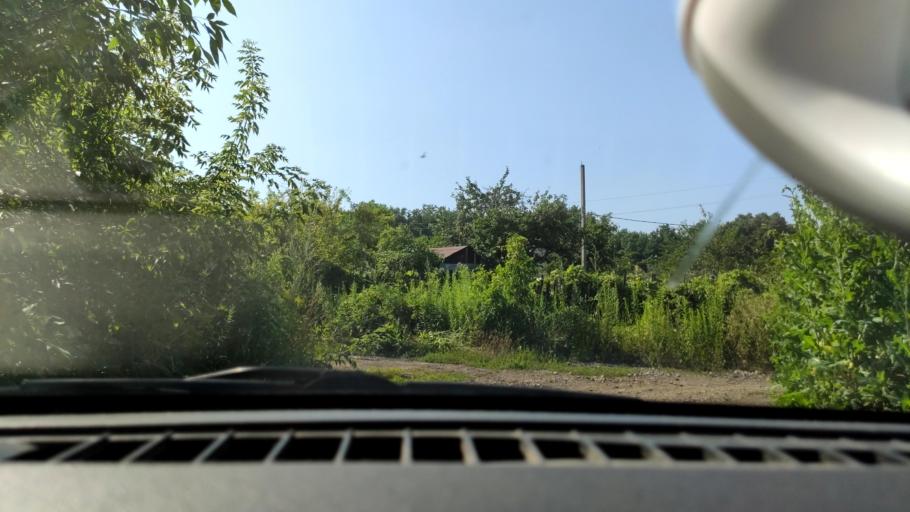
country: RU
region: Samara
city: Petra-Dubrava
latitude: 53.2689
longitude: 50.2971
